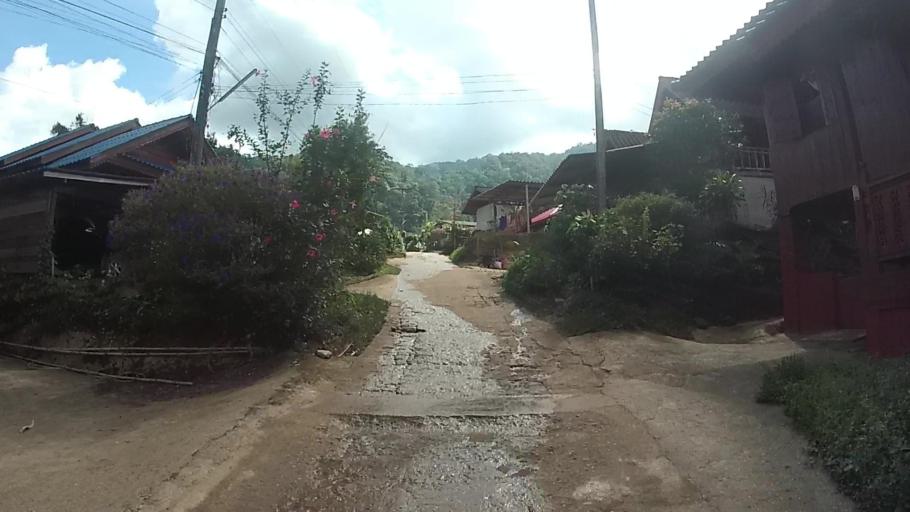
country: TH
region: Lampang
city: Mueang Pan
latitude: 18.9090
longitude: 99.4087
